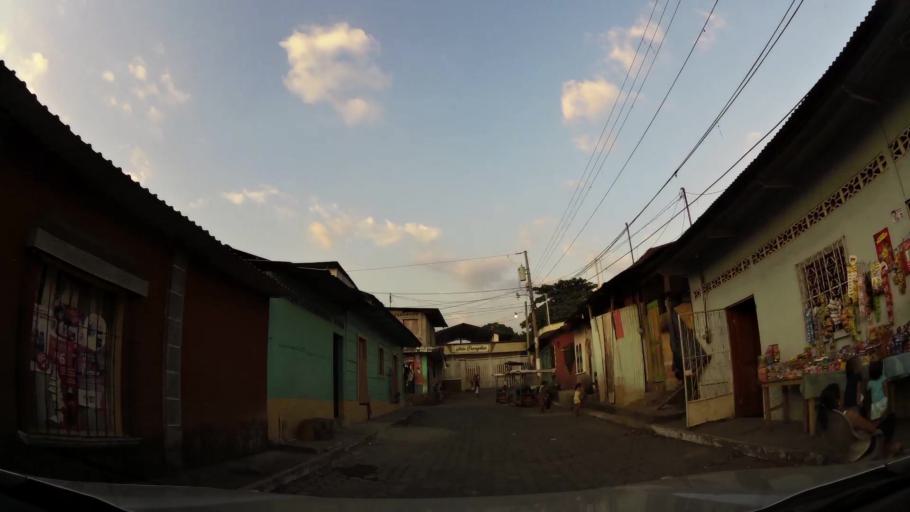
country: GT
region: Retalhuleu
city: San Sebastian
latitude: 14.5642
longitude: -91.6468
